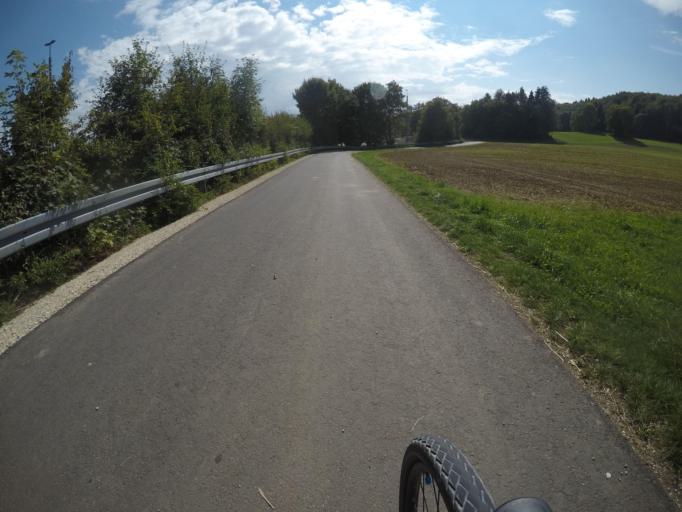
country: DE
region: Baden-Wuerttemberg
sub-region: Tuebingen Region
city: Munsingen
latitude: 48.3799
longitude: 9.5140
